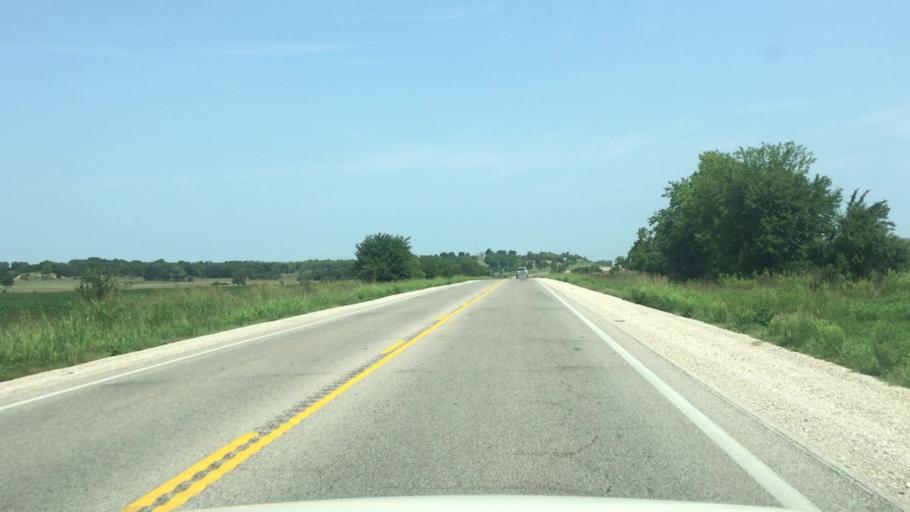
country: US
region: Kansas
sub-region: Montgomery County
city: Cherryvale
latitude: 37.1980
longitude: -95.5824
